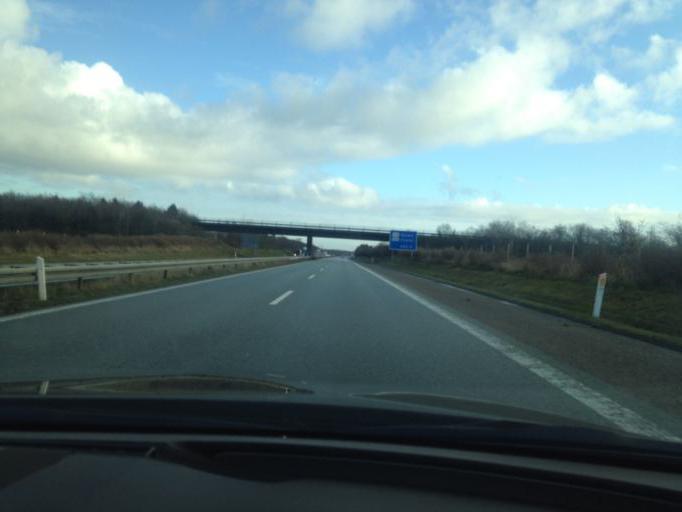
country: DK
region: South Denmark
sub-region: Vejen Kommune
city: Vejen
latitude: 55.4950
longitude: 9.1111
